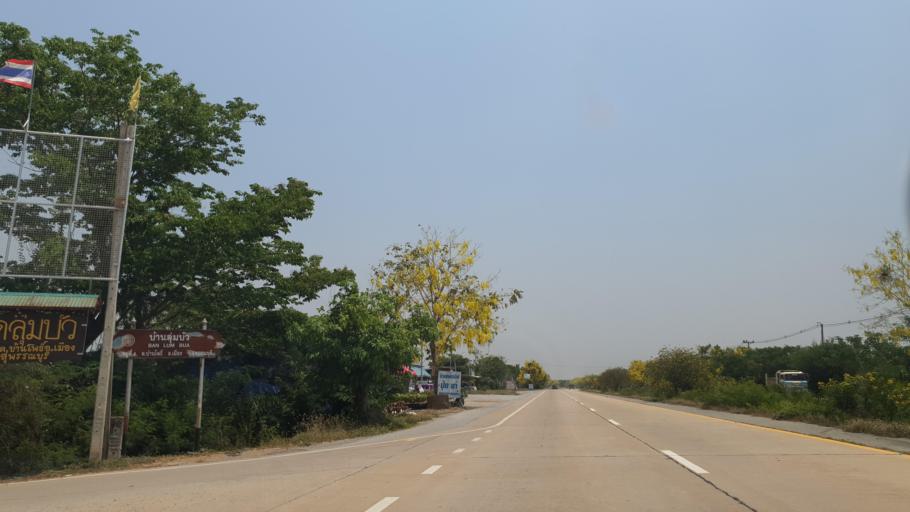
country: TH
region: Suphan Buri
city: Suphan Buri
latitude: 14.5291
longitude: 100.0598
